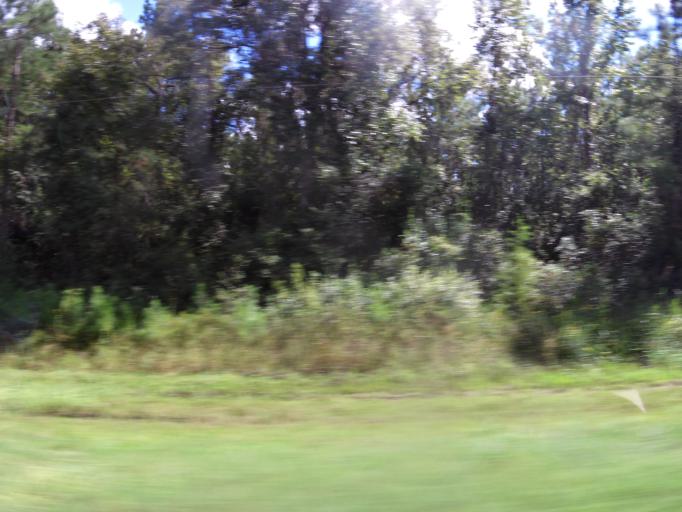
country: US
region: Florida
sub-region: Hamilton County
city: Jasper
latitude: 30.6297
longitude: -82.6007
